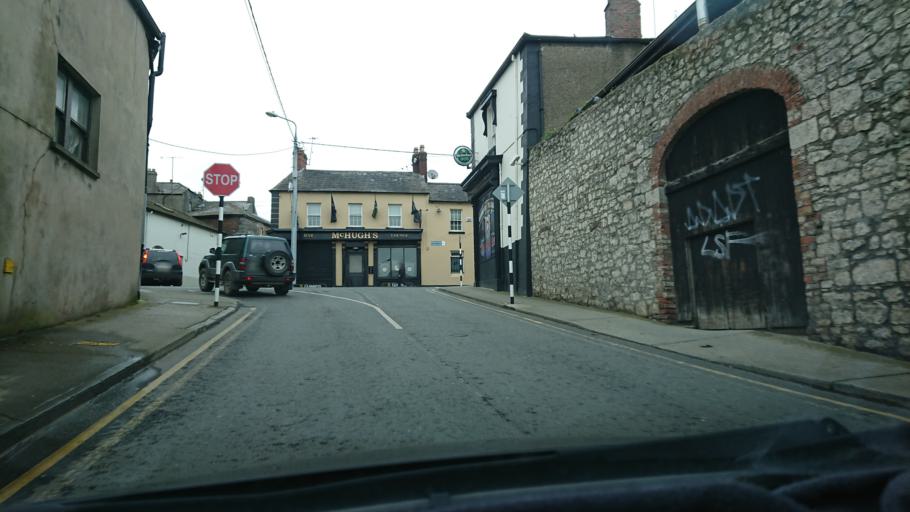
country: IE
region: Leinster
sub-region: Lu
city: Drogheda
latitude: 53.7158
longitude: -6.3466
